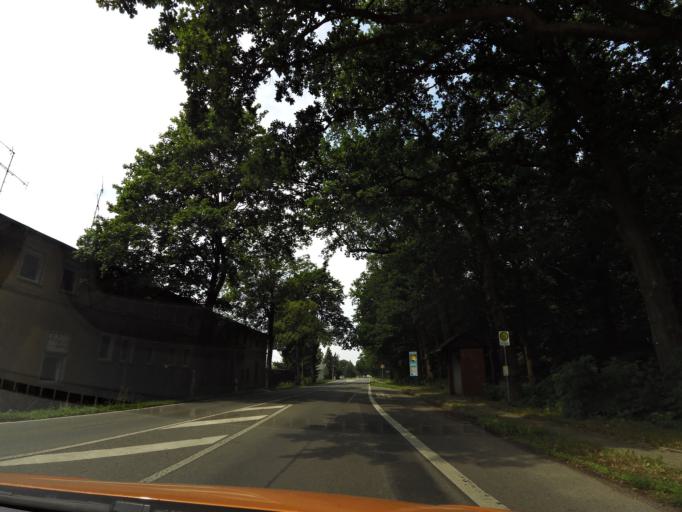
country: DE
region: Brandenburg
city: Wusterhausen
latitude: 52.9157
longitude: 12.4354
